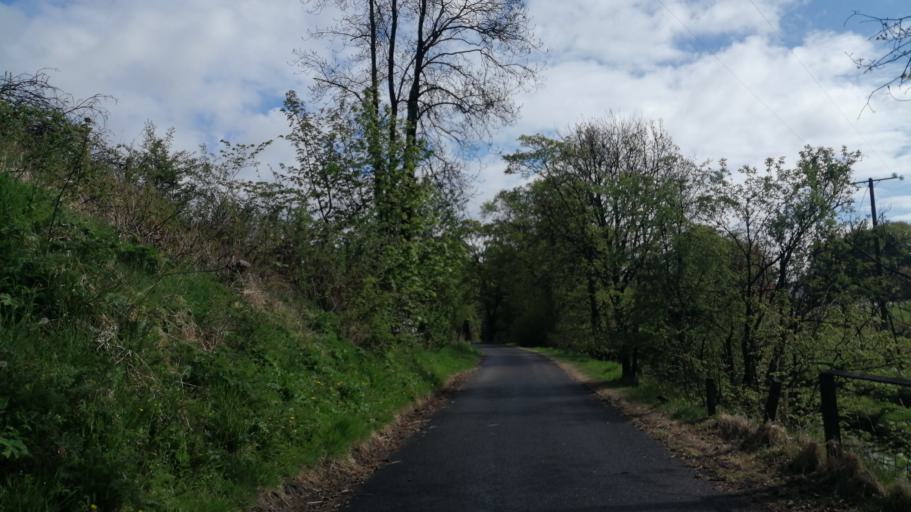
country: GB
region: Scotland
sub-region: Moray
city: Keith
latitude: 57.5410
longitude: -2.9618
